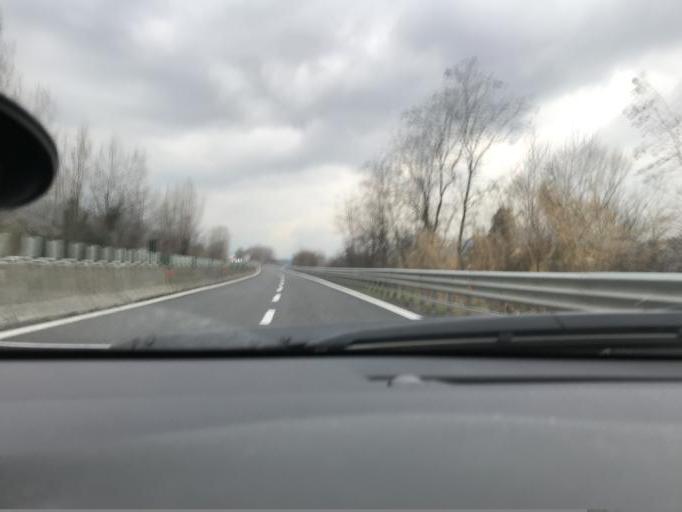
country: IT
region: The Marches
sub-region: Provincia di Ancona
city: Macine-Borgo Loreto
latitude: 43.4909
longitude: 13.1039
